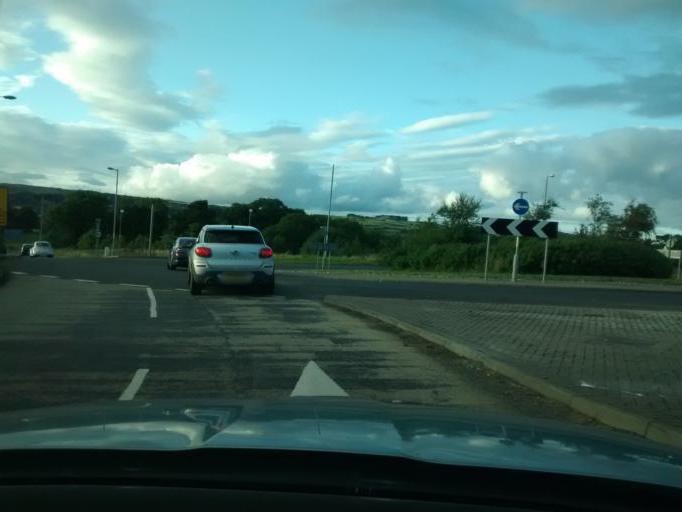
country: GB
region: Scotland
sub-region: Renfrewshire
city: Lochwinnoch
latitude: 55.7849
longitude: -4.6079
